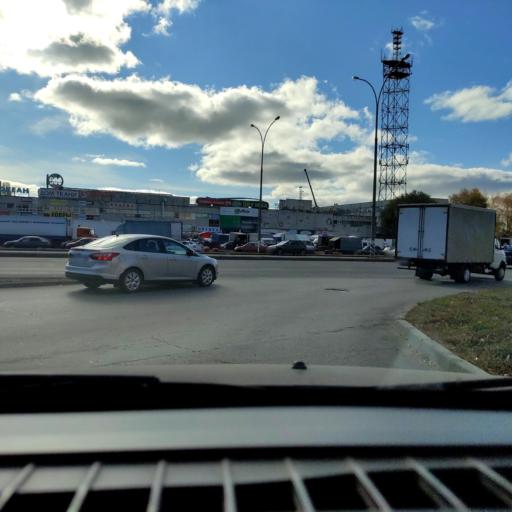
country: RU
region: Samara
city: Tol'yatti
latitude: 53.5311
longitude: 49.2650
